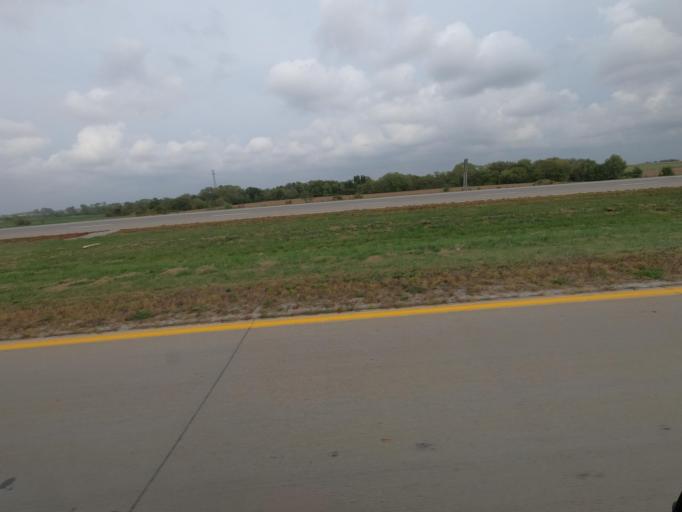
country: US
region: Iowa
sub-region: Wapello County
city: Ottumwa
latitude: 41.0618
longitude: -92.3761
